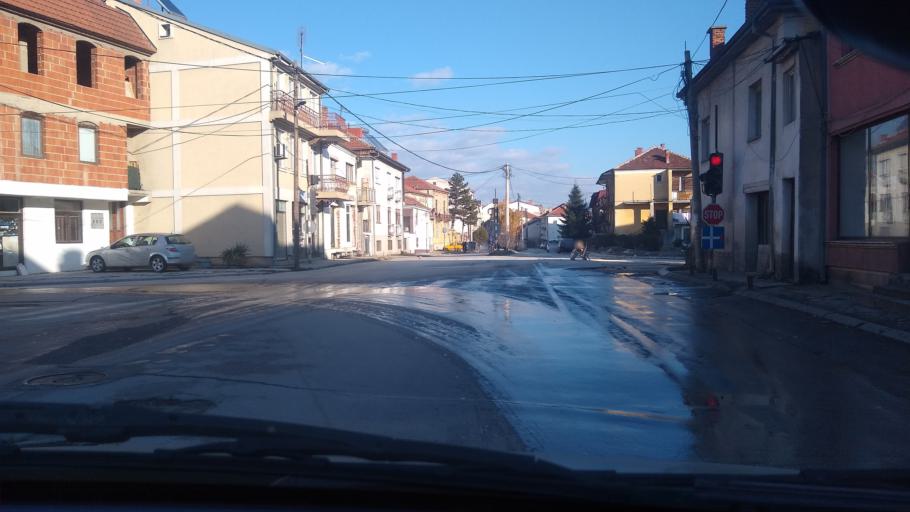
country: MK
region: Bitola
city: Bitola
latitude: 41.0252
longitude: 21.3333
